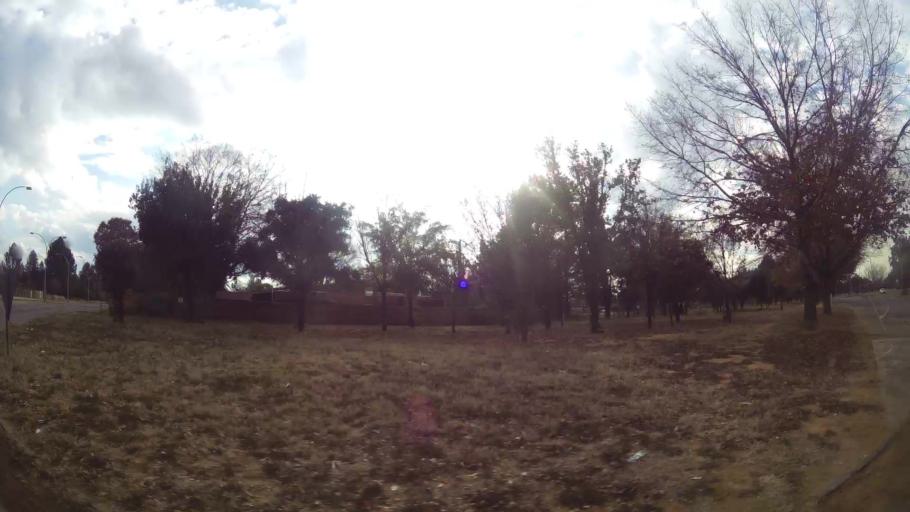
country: ZA
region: Orange Free State
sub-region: Fezile Dabi District Municipality
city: Sasolburg
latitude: -26.8028
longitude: 27.8294
